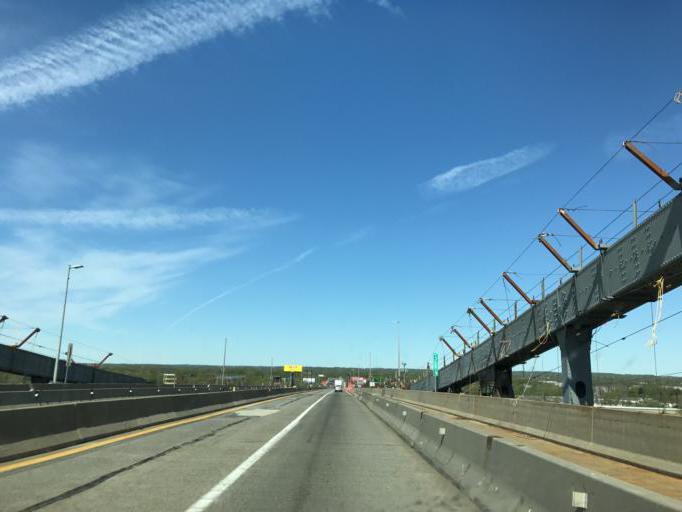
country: US
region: Pennsylvania
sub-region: Bucks County
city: Bristol
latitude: 40.1175
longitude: -74.8319
